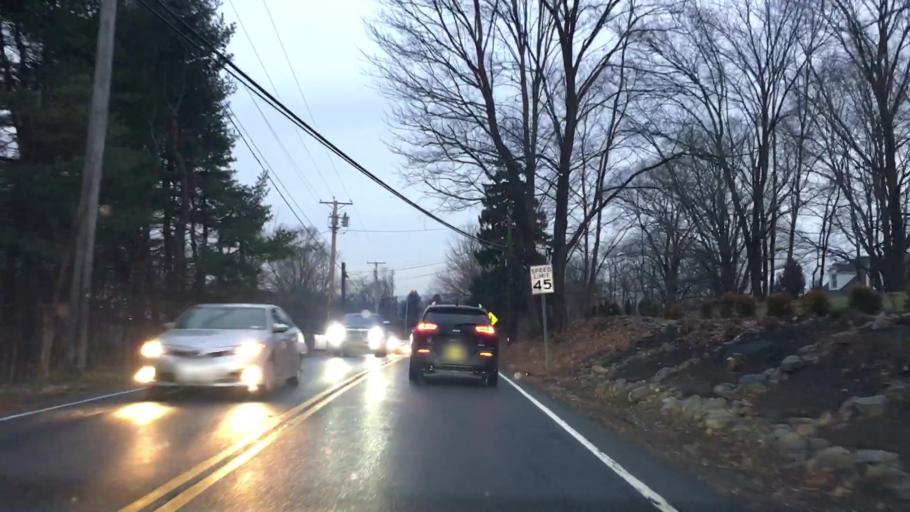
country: US
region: New York
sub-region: Dutchess County
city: Red Oaks Mill
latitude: 41.6537
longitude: -73.8405
